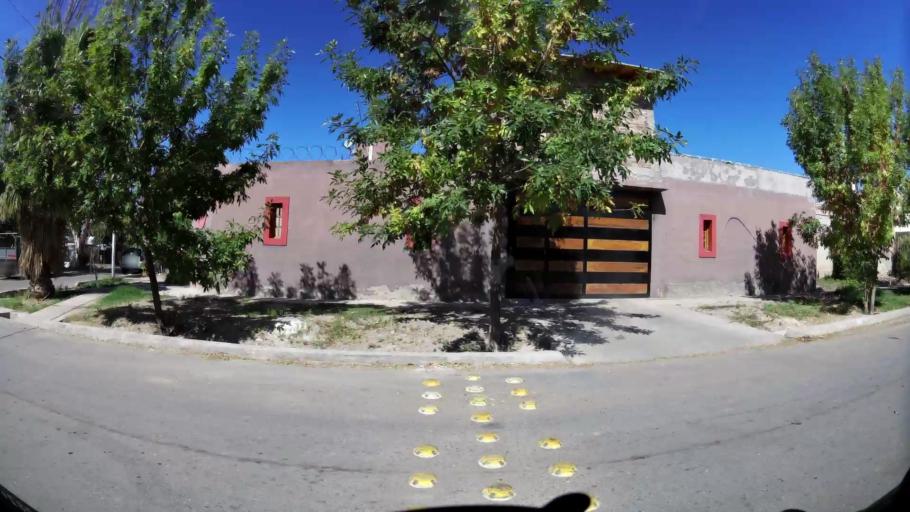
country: AR
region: Mendoza
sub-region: Departamento de Godoy Cruz
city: Godoy Cruz
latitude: -32.9541
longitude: -68.8250
